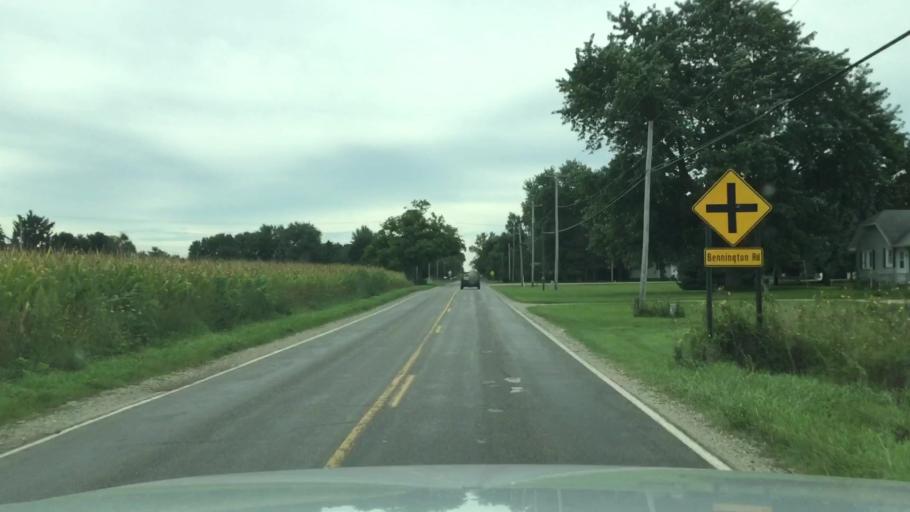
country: US
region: Michigan
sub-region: Shiawassee County
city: Durand
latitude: 42.9410
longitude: -83.9887
